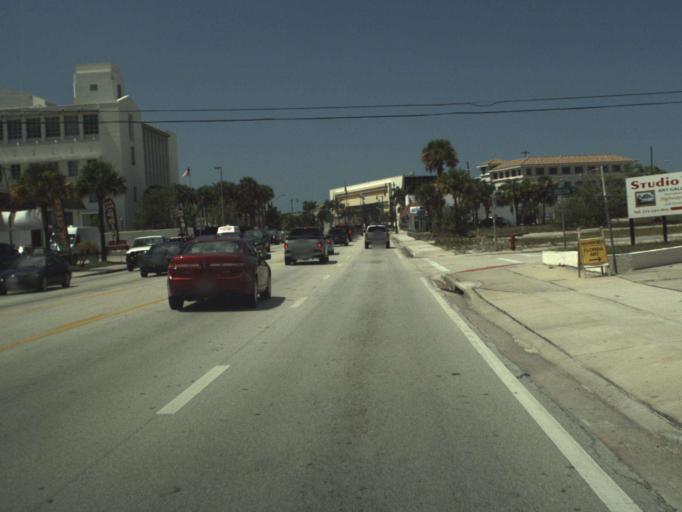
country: US
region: Florida
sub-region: Saint Lucie County
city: Fort Pierce
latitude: 27.4446
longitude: -80.3258
